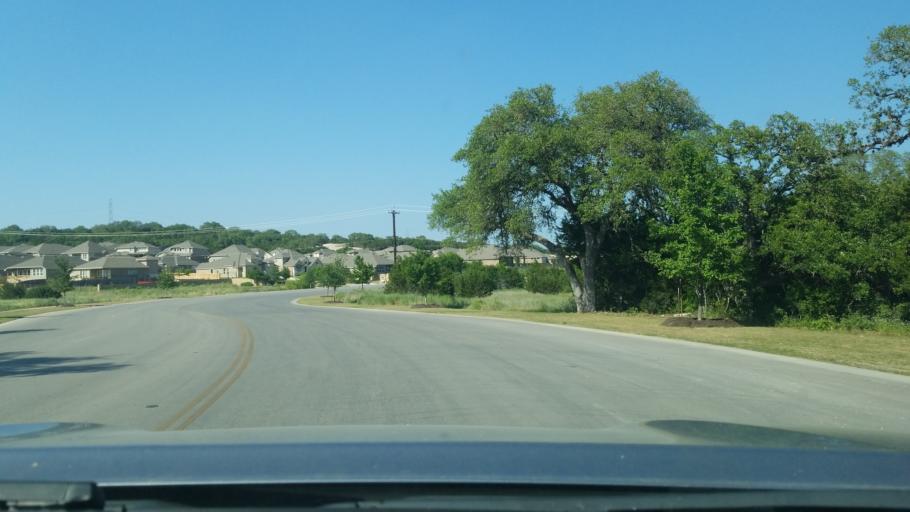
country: US
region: Texas
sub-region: Comal County
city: Bulverde
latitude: 29.7704
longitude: -98.4184
